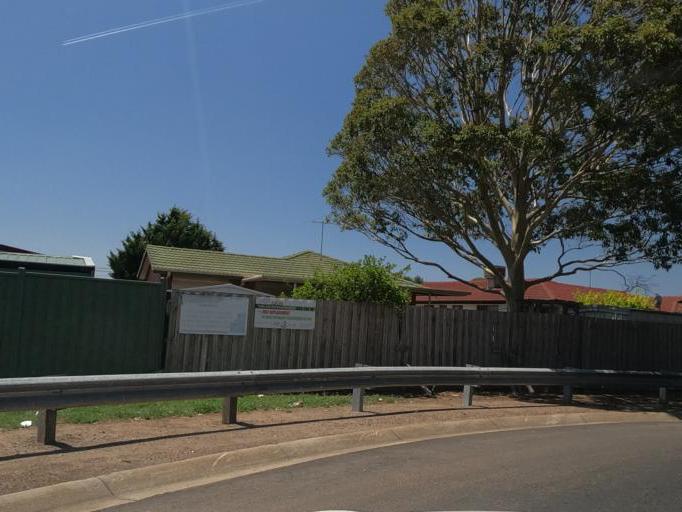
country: AU
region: Victoria
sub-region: Hume
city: Broadmeadows
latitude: -37.6745
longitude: 144.9201
